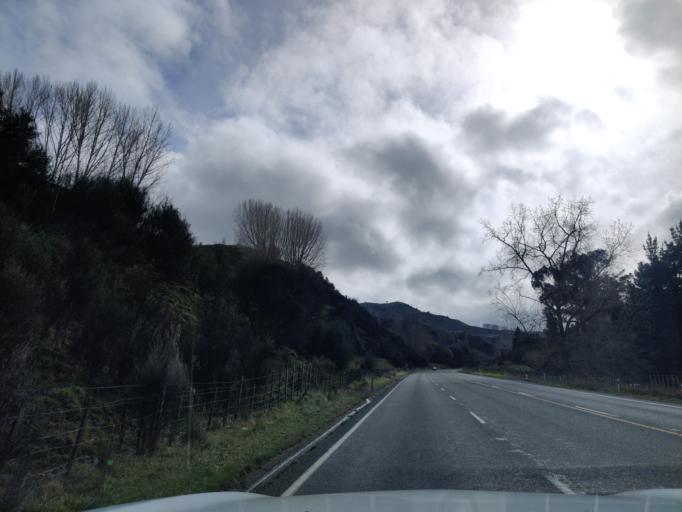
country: NZ
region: Manawatu-Wanganui
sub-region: Ruapehu District
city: Waiouru
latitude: -39.7824
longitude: 175.7863
